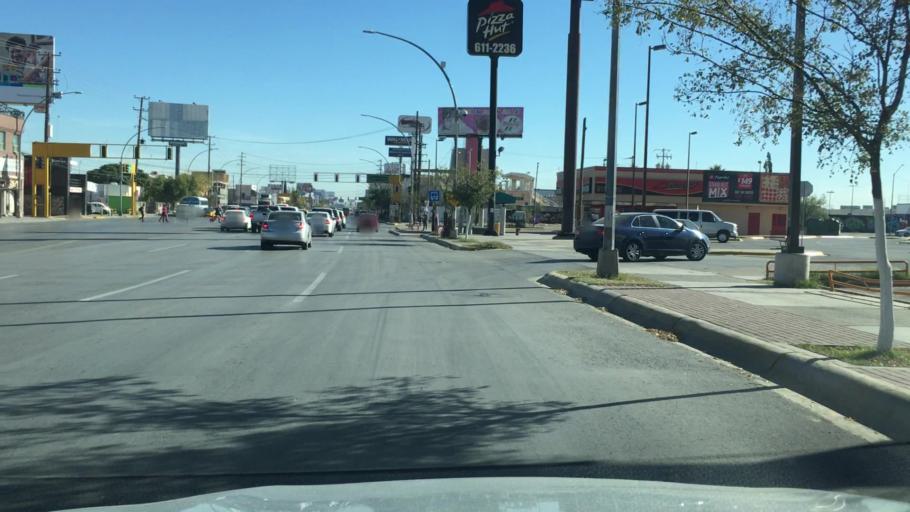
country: MX
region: Chihuahua
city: Ciudad Juarez
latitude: 31.7367
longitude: -106.4463
